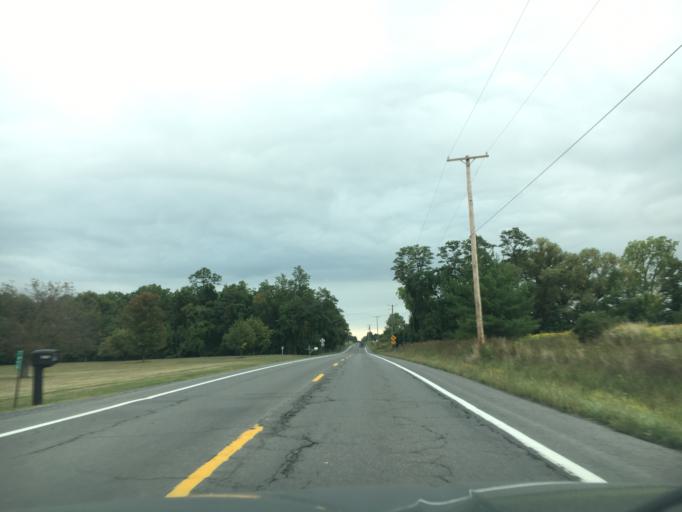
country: US
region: New York
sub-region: Tompkins County
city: Trumansburg
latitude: 42.6639
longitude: -76.7263
